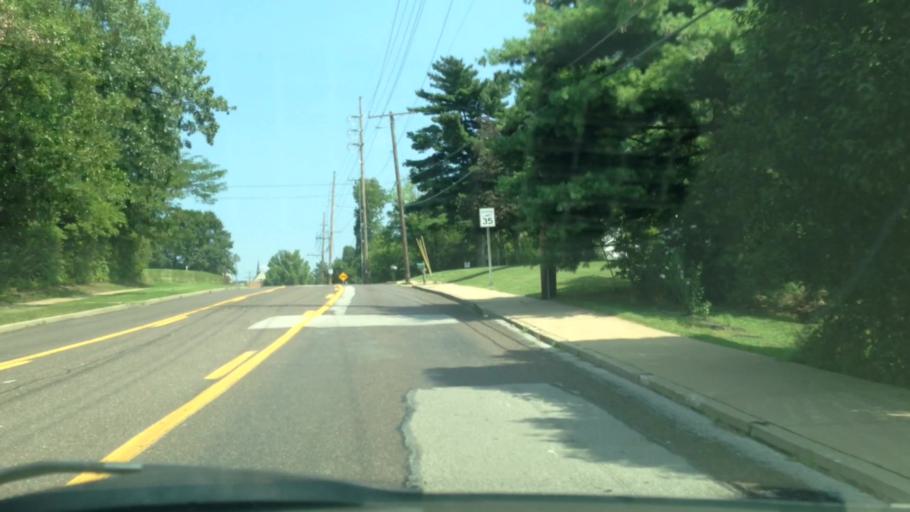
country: US
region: Missouri
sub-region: Saint Louis County
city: Des Peres
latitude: 38.5990
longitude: -90.4439
